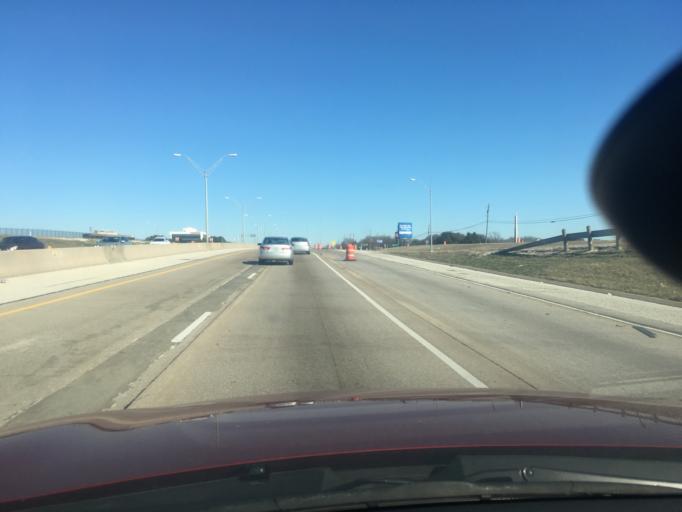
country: US
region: Texas
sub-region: Dallas County
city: Duncanville
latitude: 32.6727
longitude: -96.8604
